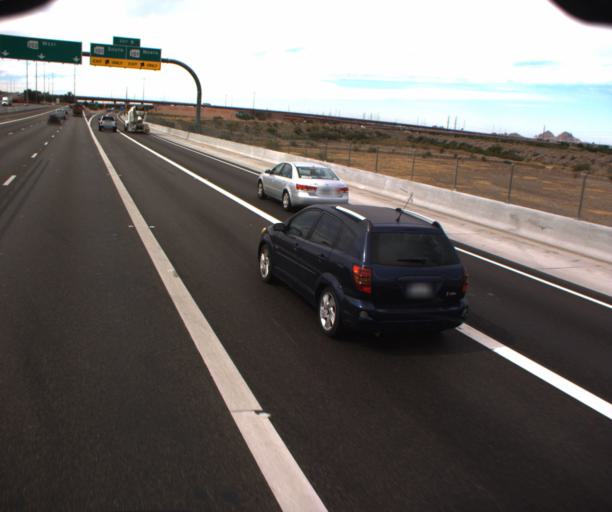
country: US
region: Arizona
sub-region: Maricopa County
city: Tempe
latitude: 33.4351
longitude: -111.8804
